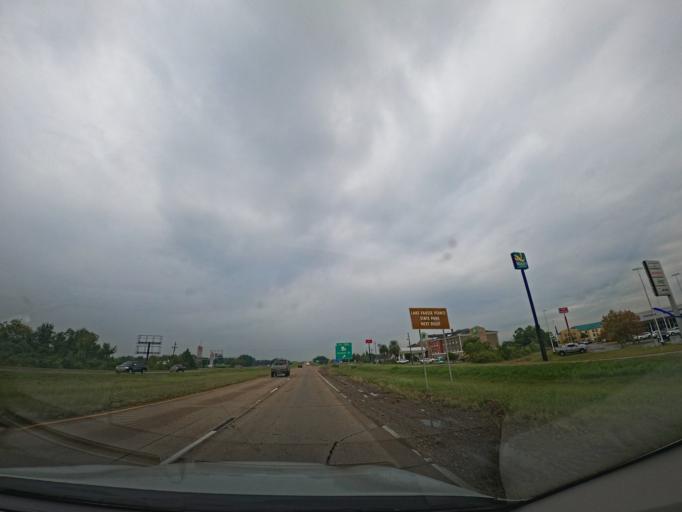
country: US
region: Louisiana
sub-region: Iberia Parish
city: New Iberia
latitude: 29.9819
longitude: -91.8548
